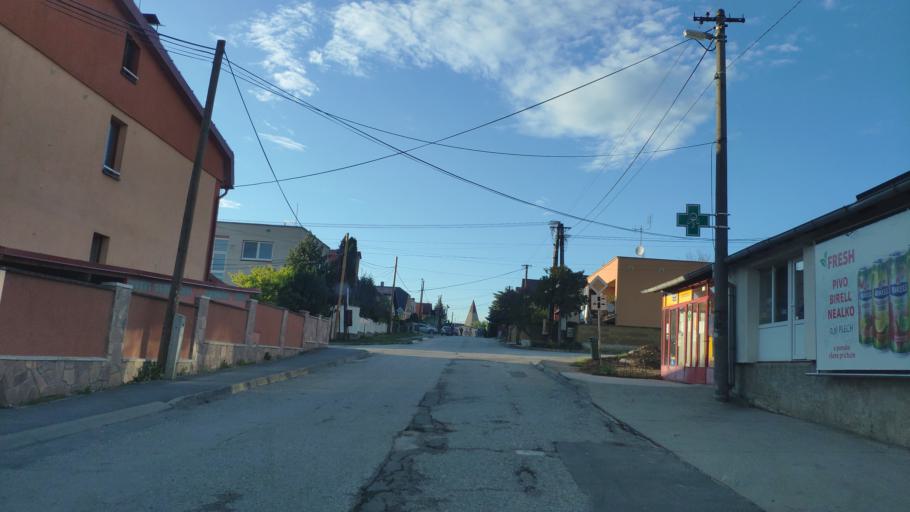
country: SK
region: Kosicky
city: Kosice
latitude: 48.7498
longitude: 21.3475
